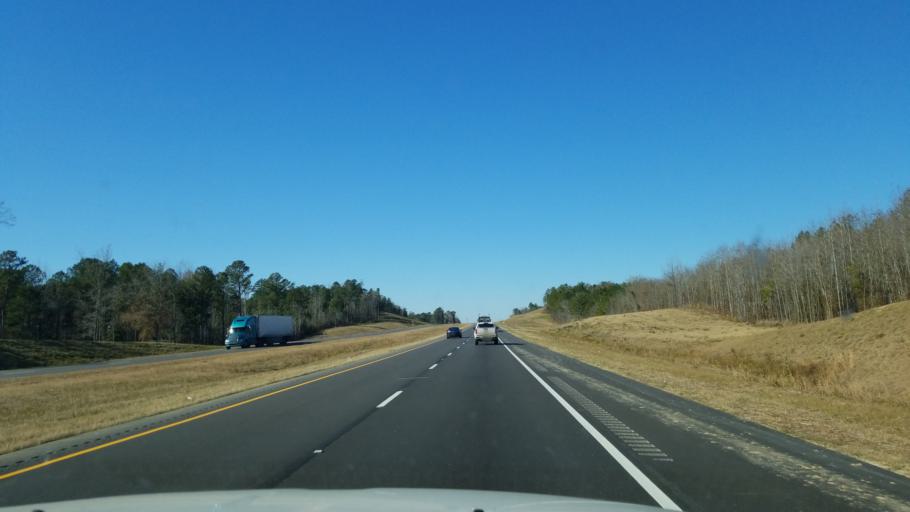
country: US
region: Alabama
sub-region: Pickens County
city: Reform
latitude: 33.3550
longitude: -87.9648
